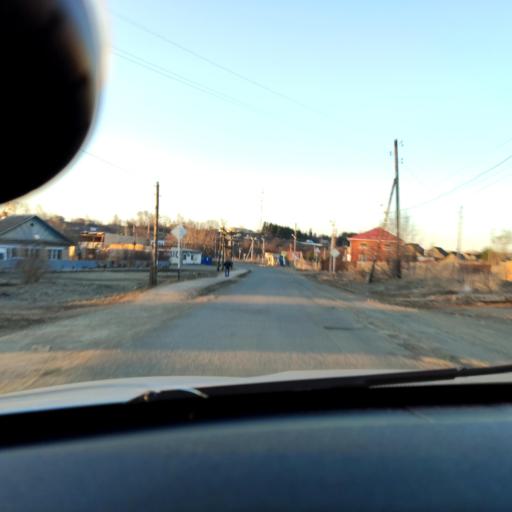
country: RU
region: Perm
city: Kultayevo
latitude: 57.9295
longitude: 55.8767
